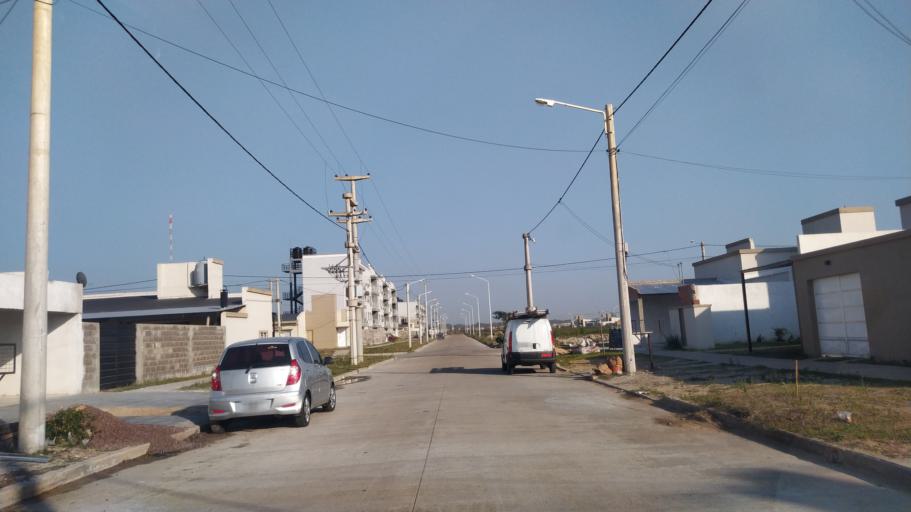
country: AR
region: Corrientes
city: Corrientes
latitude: -27.5278
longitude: -58.8044
